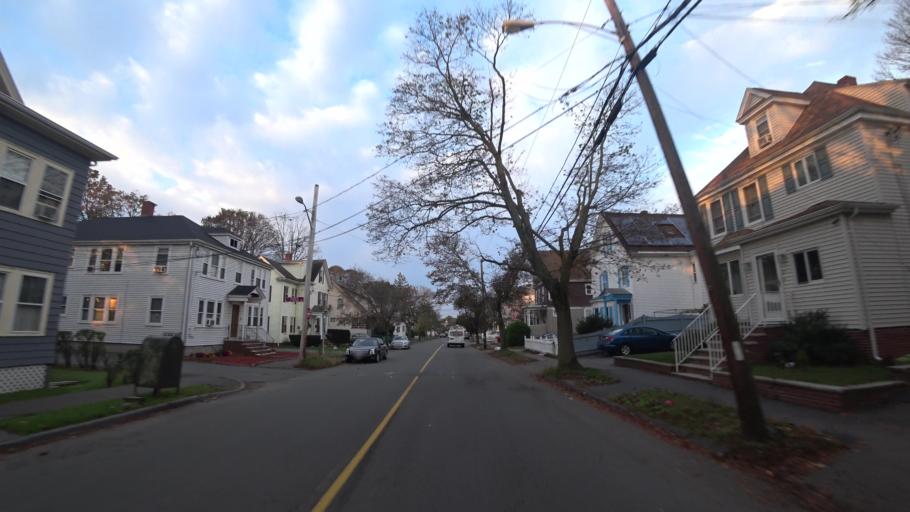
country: US
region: Massachusetts
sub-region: Essex County
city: Saugus
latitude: 42.4507
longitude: -71.0064
